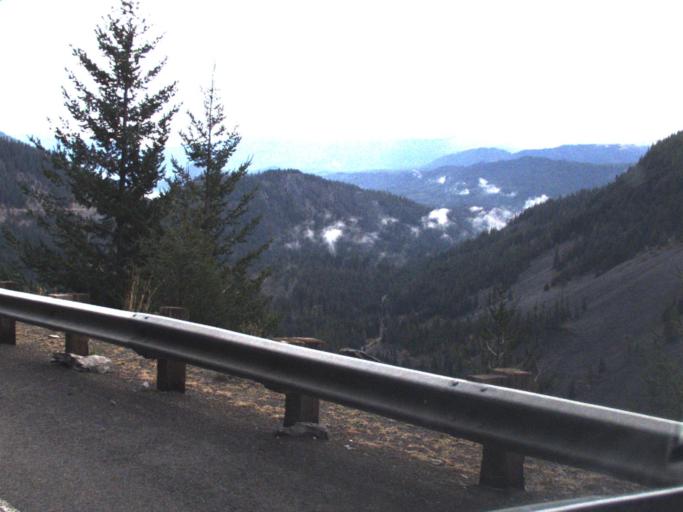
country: US
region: Washington
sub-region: Yakima County
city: Tieton
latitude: 46.6565
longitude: -121.3333
